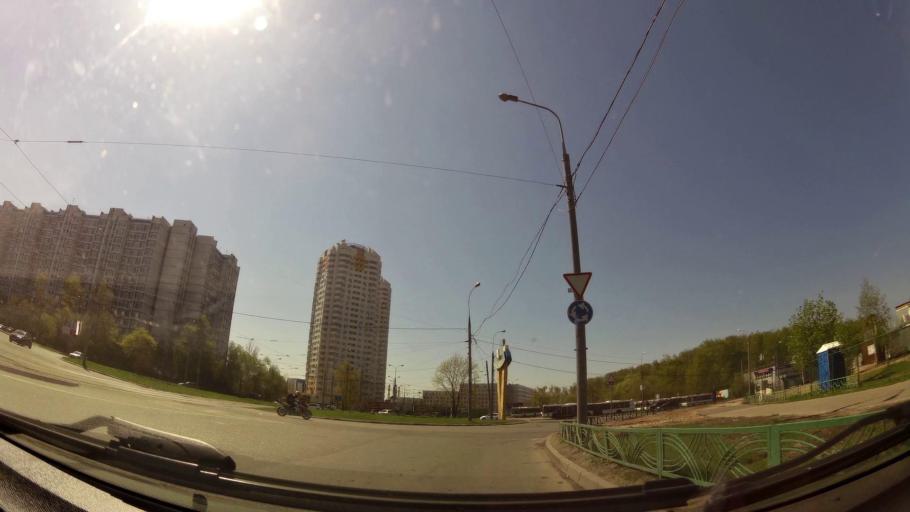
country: RU
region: Moscow
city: Strogino
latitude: 55.8009
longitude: 37.3906
